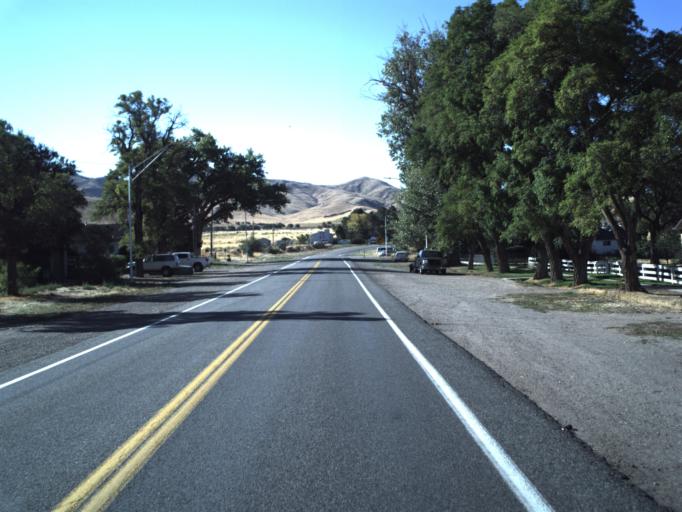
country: US
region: Utah
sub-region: Millard County
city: Delta
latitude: 39.3721
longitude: -112.3361
